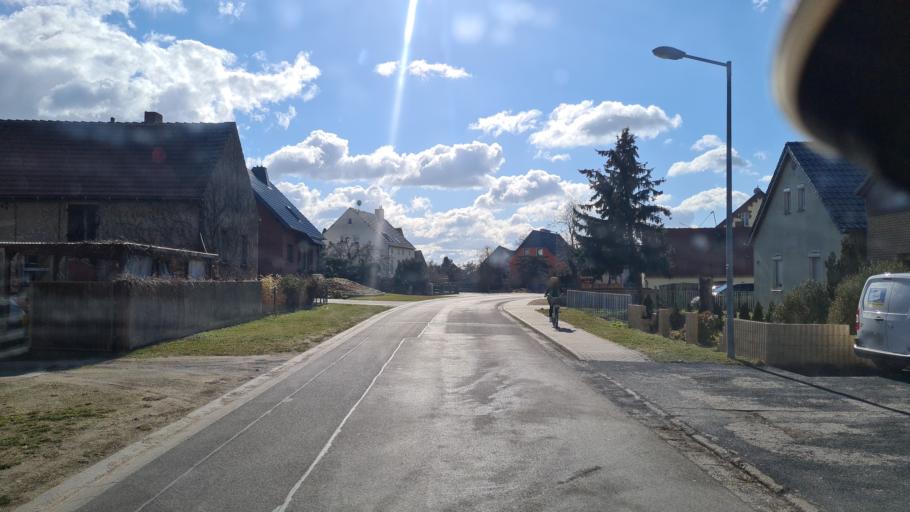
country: DE
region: Brandenburg
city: Falkenberg
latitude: 51.5808
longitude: 13.2105
